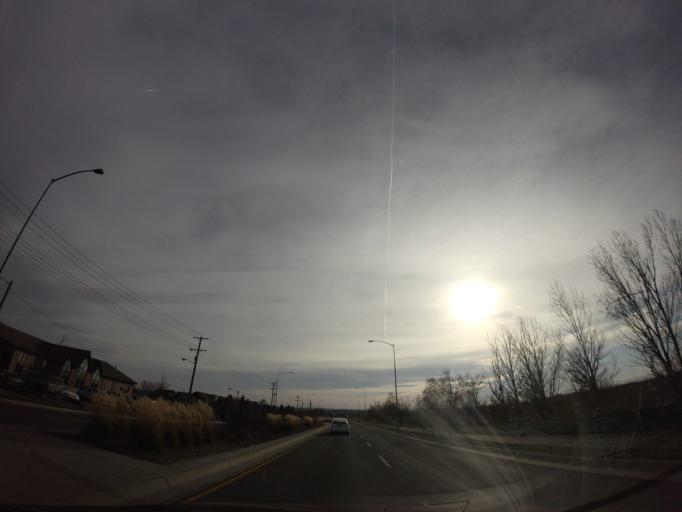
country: US
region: Montana
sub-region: Yellowstone County
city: Billings
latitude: 45.7424
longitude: -108.6175
